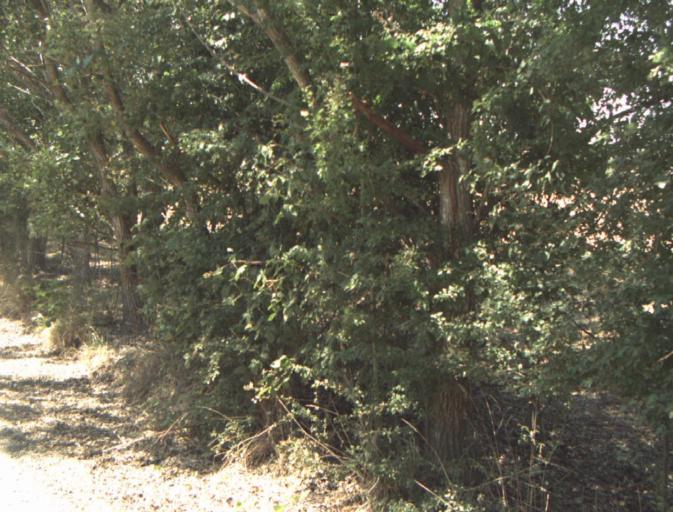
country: AU
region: Tasmania
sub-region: Launceston
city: Newstead
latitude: -41.4909
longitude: 147.2114
